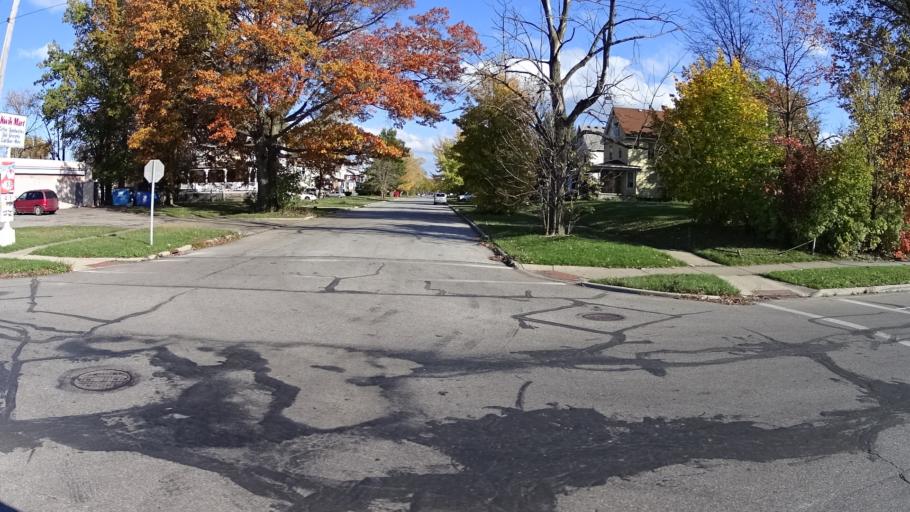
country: US
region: Ohio
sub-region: Lorain County
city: Sheffield
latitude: 41.4411
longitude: -82.1366
